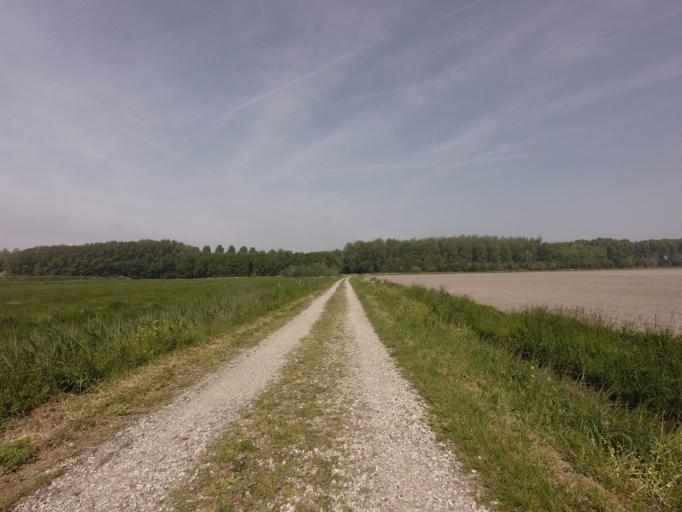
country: NL
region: South Holland
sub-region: Gemeente Hellevoetsluis
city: Hellevoetsluis
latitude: 51.8269
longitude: 4.1741
